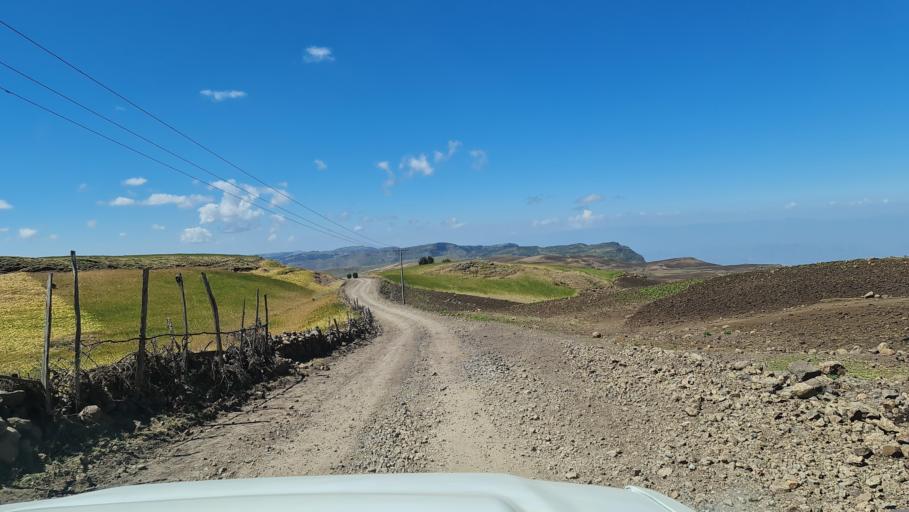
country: ET
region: Amhara
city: Debark'
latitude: 13.2296
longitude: 38.0975
